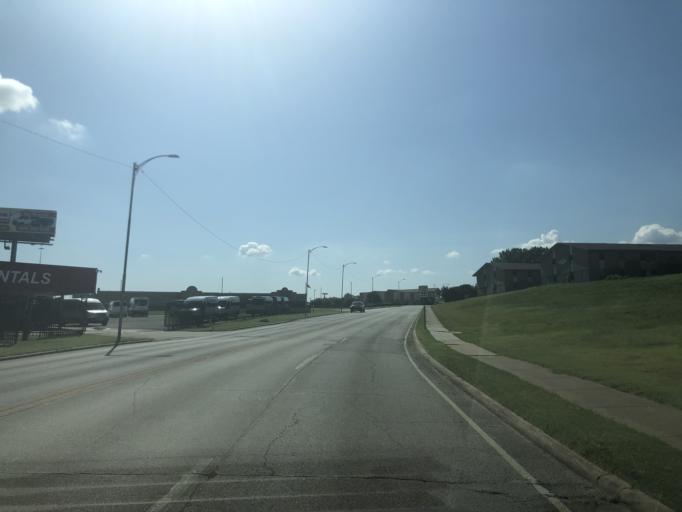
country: US
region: Texas
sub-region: Dallas County
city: Grand Prairie
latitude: 32.7588
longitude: -97.0111
